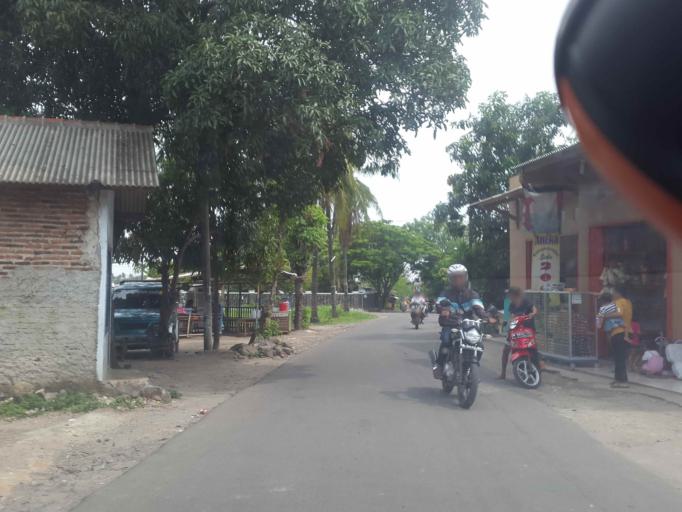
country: ID
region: Banten
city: Pangarengan
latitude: -5.9914
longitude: 106.0599
